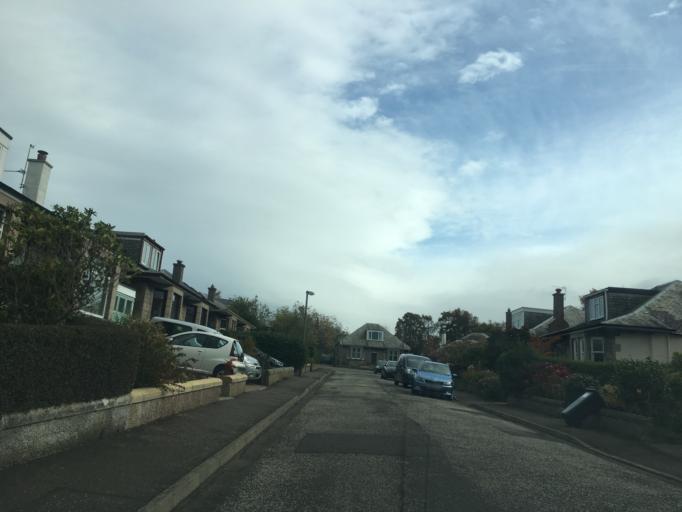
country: GB
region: Scotland
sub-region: Edinburgh
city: Colinton
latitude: 55.9161
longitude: -3.2198
